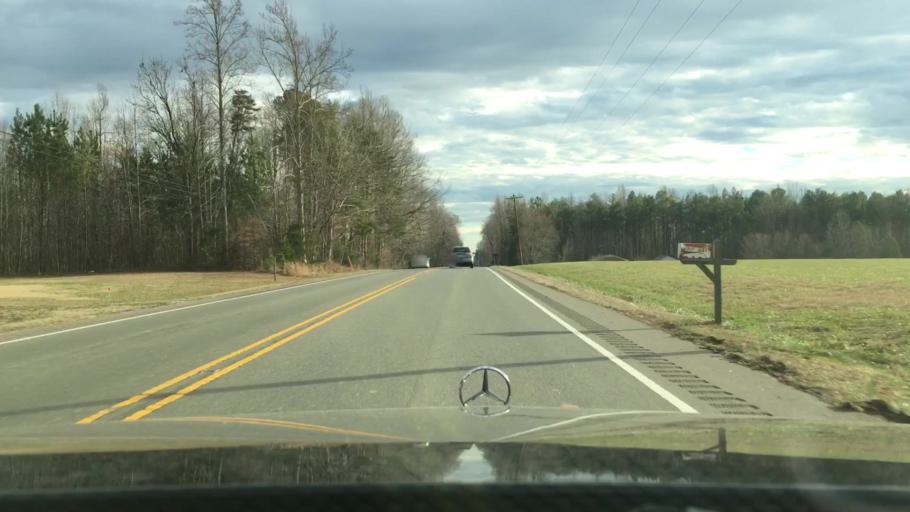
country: US
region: North Carolina
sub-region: Orange County
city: Hillsborough
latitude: 36.1894
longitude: -79.1385
